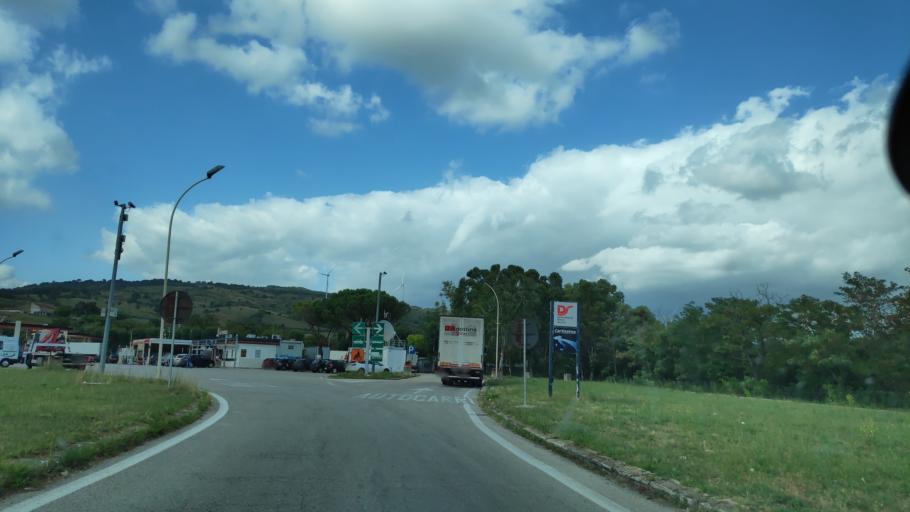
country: IT
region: Campania
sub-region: Provincia di Salerno
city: Serre
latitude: 40.6230
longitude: 15.1823
